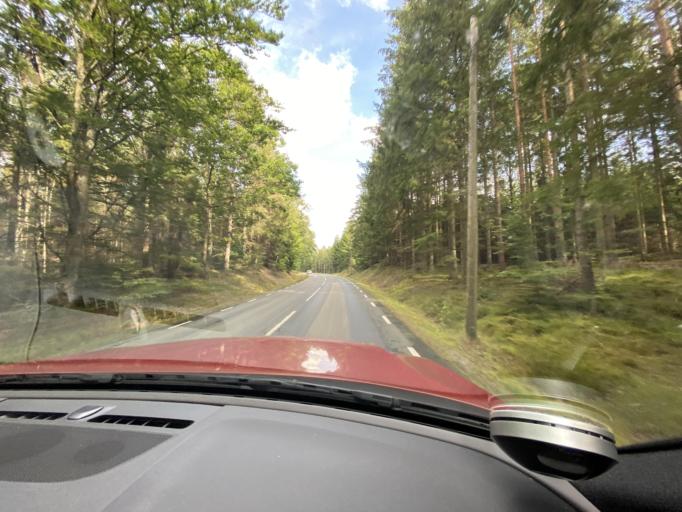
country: SE
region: Skane
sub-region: Hassleholms Kommun
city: Bjarnum
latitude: 56.3389
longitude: 13.6894
